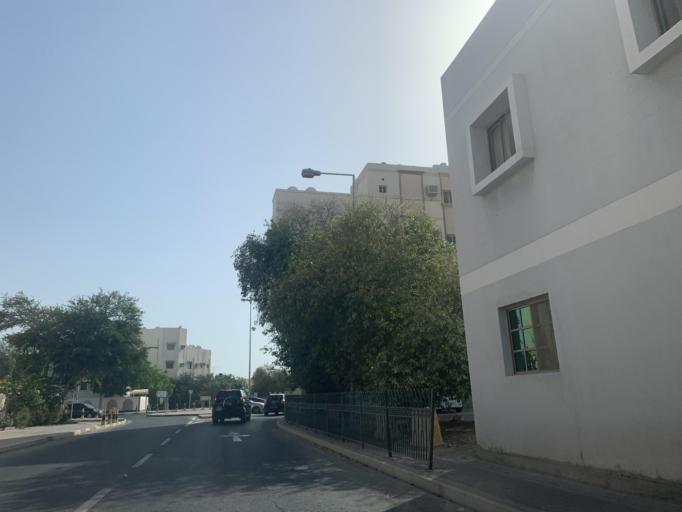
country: BH
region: Northern
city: Madinat `Isa
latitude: 26.1613
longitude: 50.5742
